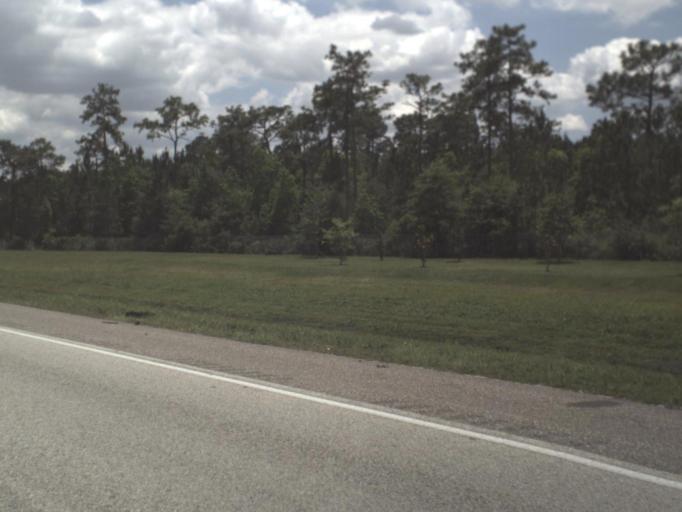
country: US
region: Florida
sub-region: Duval County
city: Jacksonville Beach
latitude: 30.2610
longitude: -81.5186
